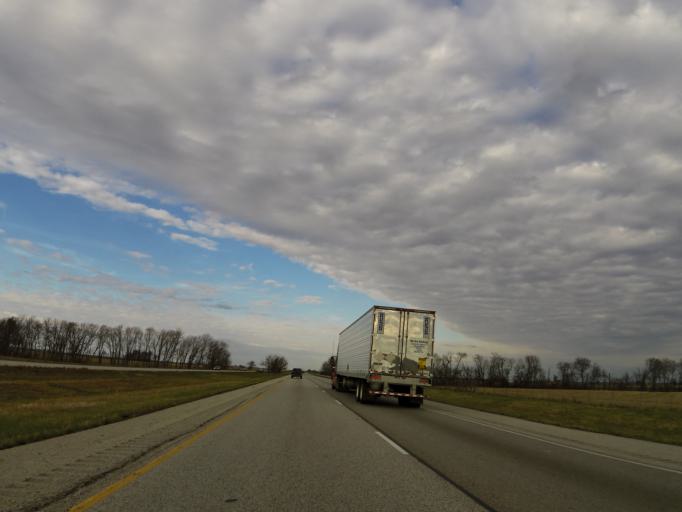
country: US
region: Illinois
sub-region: Washington County
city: Nashville
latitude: 38.4169
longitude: -89.4428
